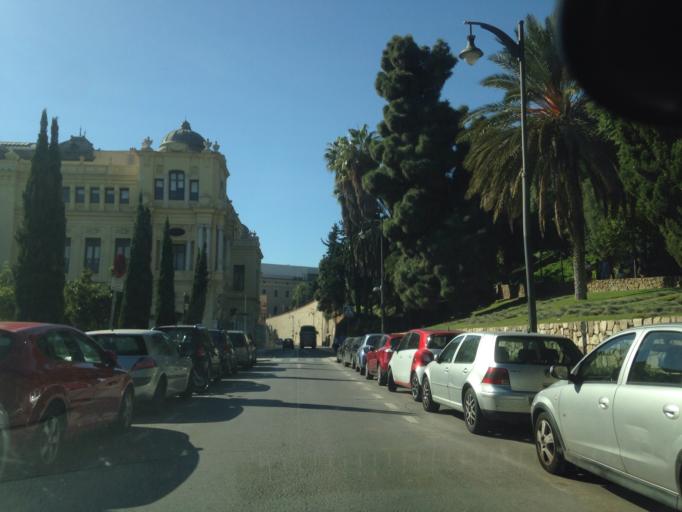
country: ES
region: Andalusia
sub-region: Provincia de Malaga
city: Malaga
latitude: 36.7209
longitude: -4.4142
